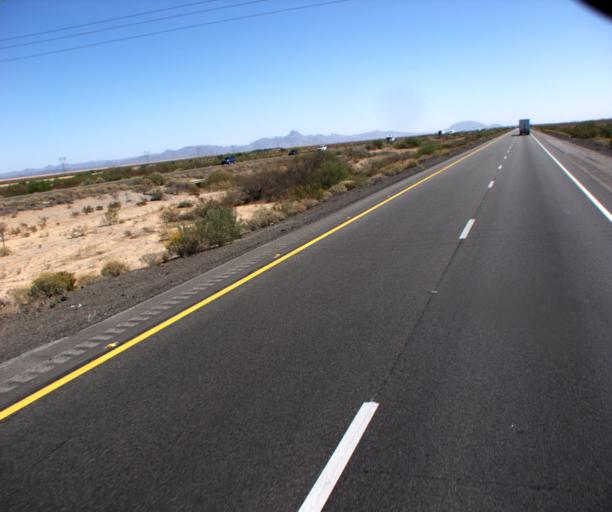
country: US
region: Arizona
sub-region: La Paz County
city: Salome
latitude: 33.5739
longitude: -113.3872
